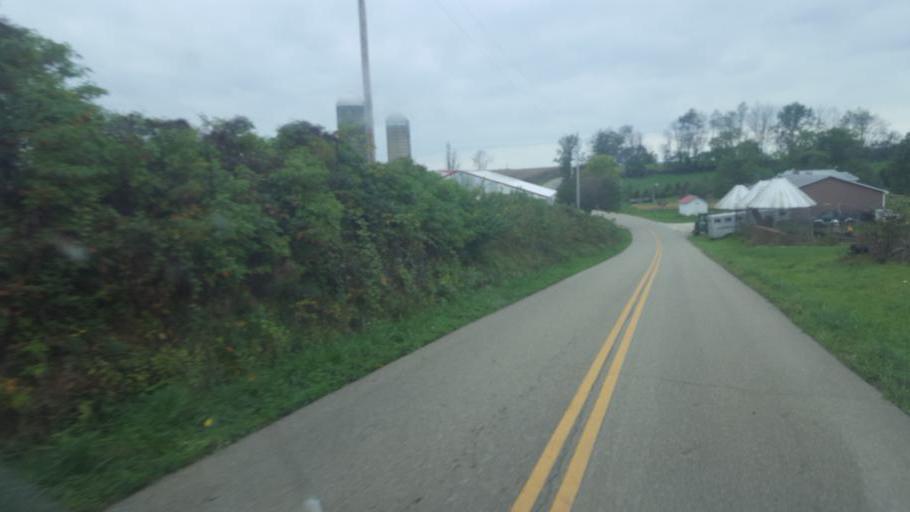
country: US
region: Ohio
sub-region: Carroll County
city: Carrollton
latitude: 40.4765
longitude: -81.0460
